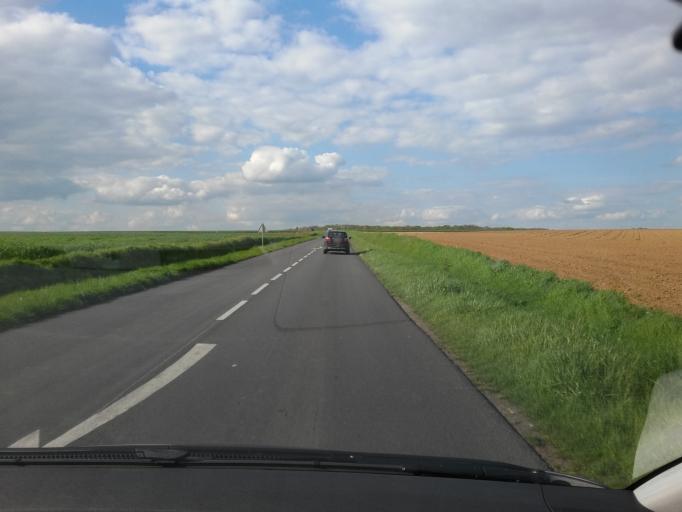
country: FR
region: Picardie
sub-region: Departement de l'Oise
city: Grandfresnoy
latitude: 49.3878
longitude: 2.6568
